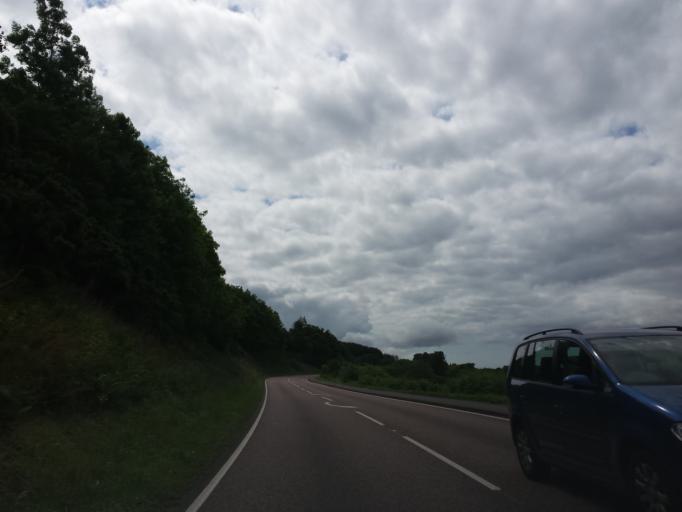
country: GB
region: Scotland
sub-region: Argyll and Bute
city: Oban
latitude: 56.4386
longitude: -5.4502
